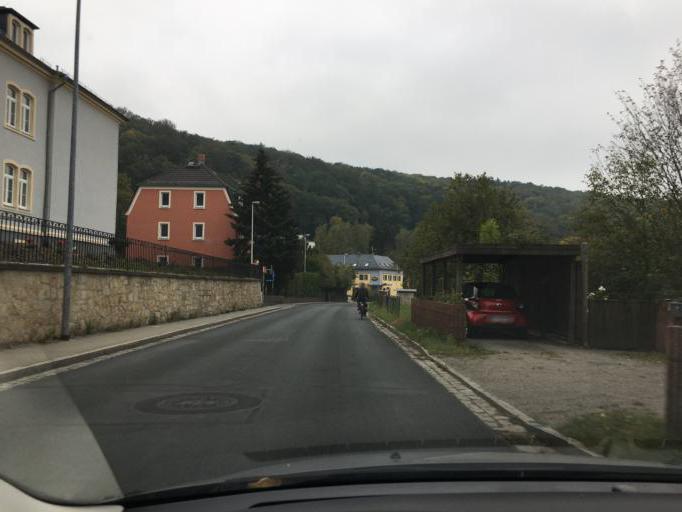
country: DE
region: Saxony
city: Freital
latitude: 51.0006
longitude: 13.6766
